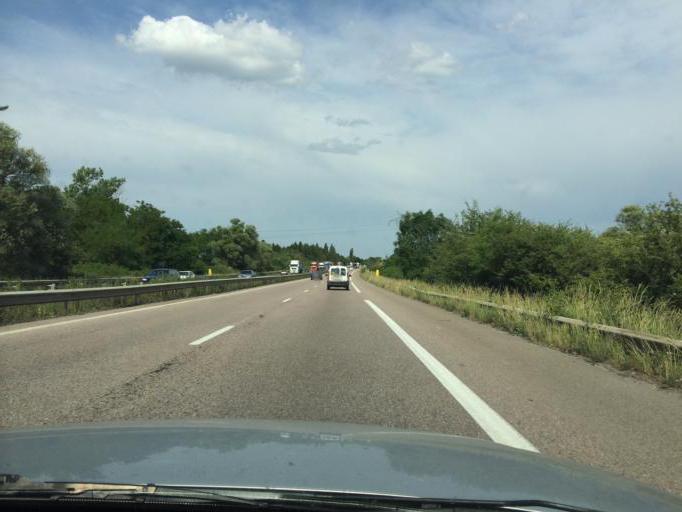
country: FR
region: Lorraine
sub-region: Departement de Meurthe-et-Moselle
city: Gondreville
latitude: 48.6835
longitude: 5.9479
